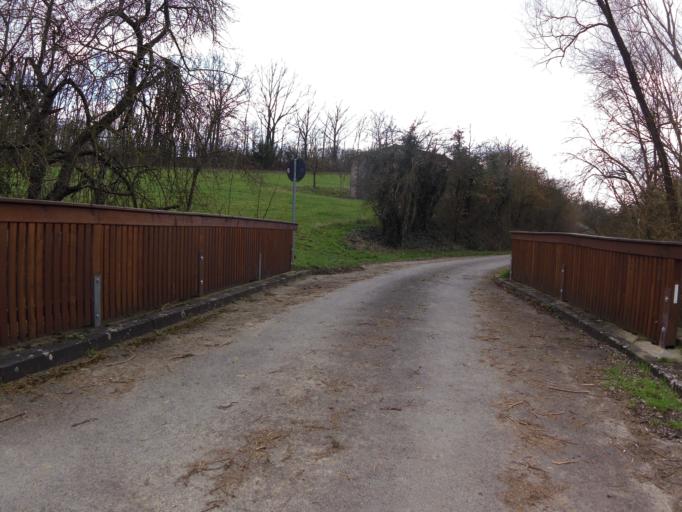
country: DE
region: Bavaria
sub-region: Regierungsbezirk Unterfranken
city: Buchbrunn
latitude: 49.7486
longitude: 10.1194
